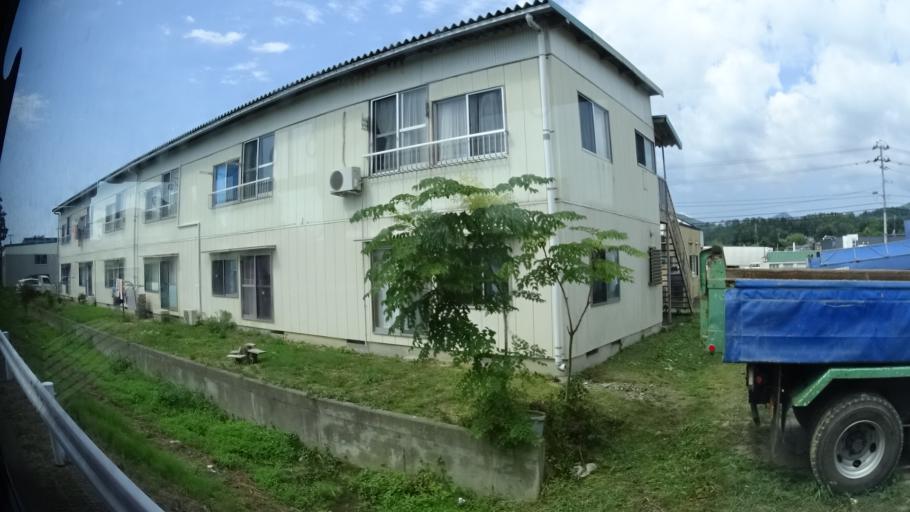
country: JP
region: Iwate
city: Ofunato
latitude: 38.8457
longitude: 141.5818
